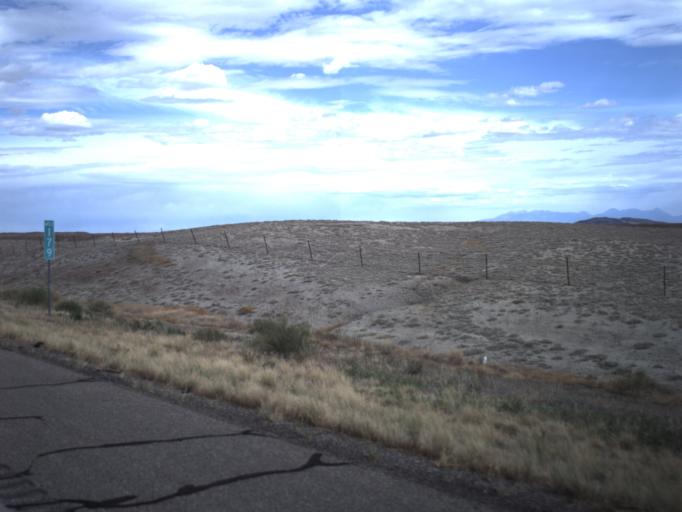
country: US
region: Utah
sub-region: Grand County
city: Moab
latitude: 38.9304
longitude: -109.8735
